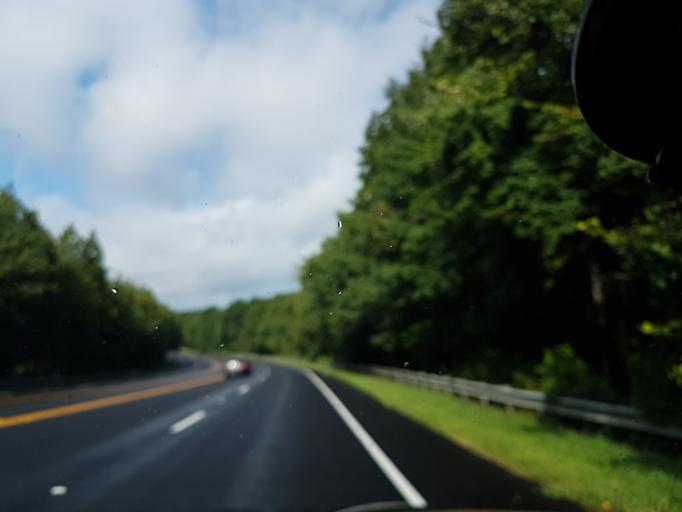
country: US
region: Georgia
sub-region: Fulton County
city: Union City
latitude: 33.5702
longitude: -84.5519
